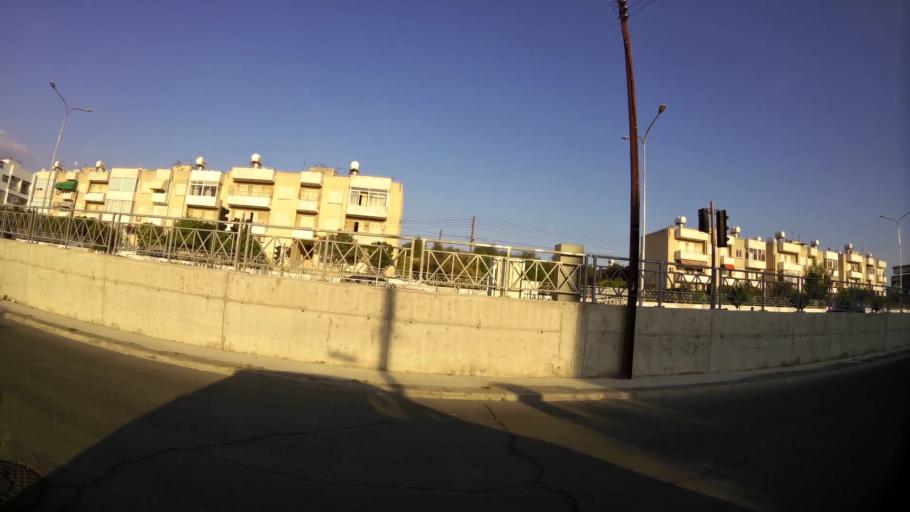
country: CY
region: Larnaka
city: Larnaca
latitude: 34.9181
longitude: 33.6003
